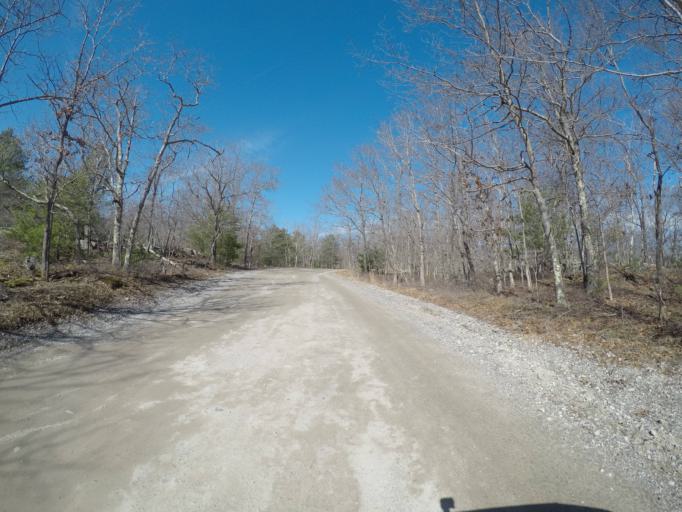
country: US
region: Massachusetts
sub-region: Norfolk County
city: Sharon
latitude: 42.0813
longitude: -71.1502
